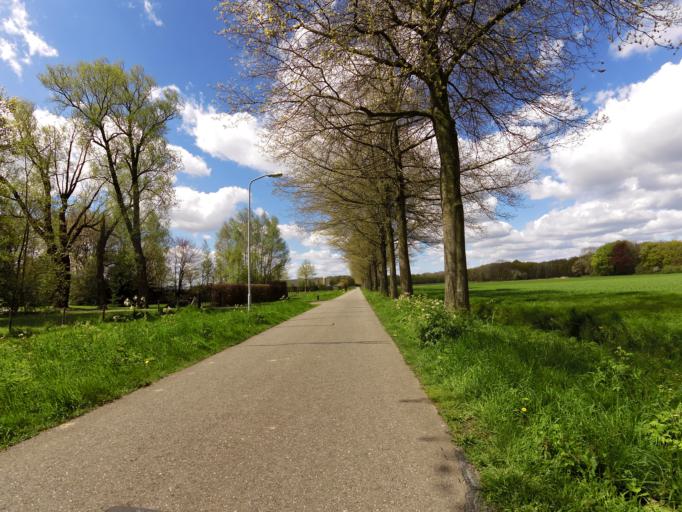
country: NL
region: Gelderland
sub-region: Gemeente Doesburg
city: Doesburg
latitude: 51.9280
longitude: 6.1710
